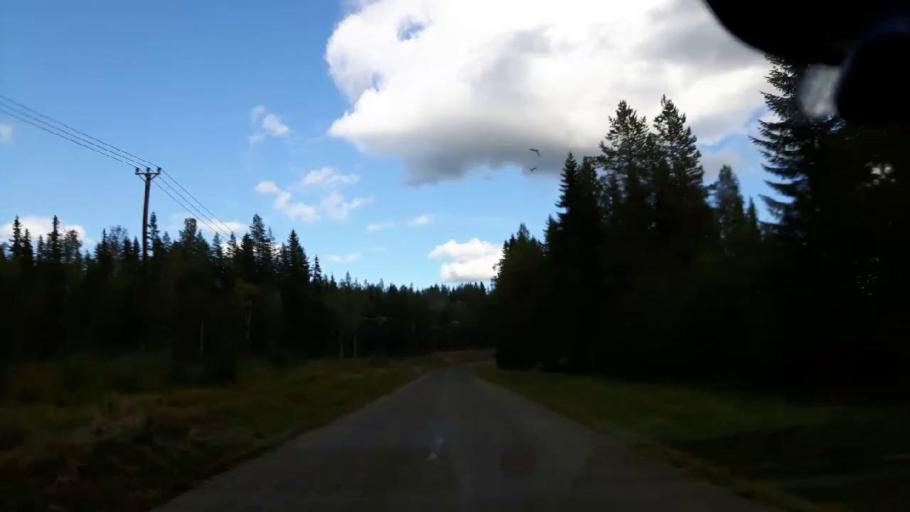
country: SE
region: Jaemtland
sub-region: Stroemsunds Kommun
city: Stroemsund
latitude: 63.4186
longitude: 15.8657
